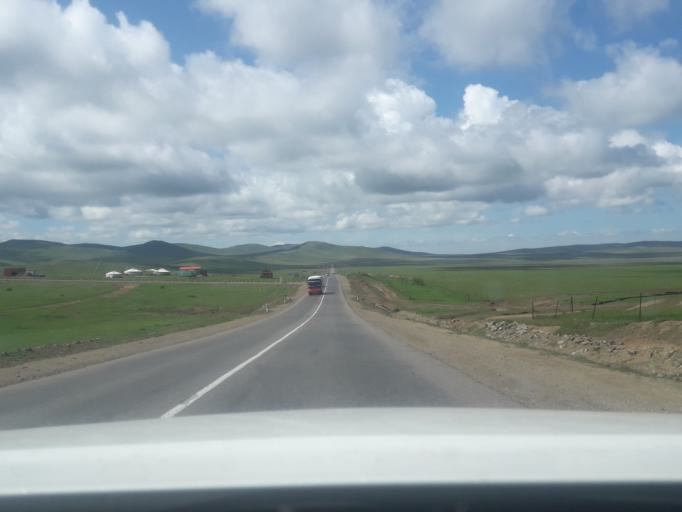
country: MN
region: Central Aimak
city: Altanbulag
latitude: 47.9008
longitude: 106.4781
